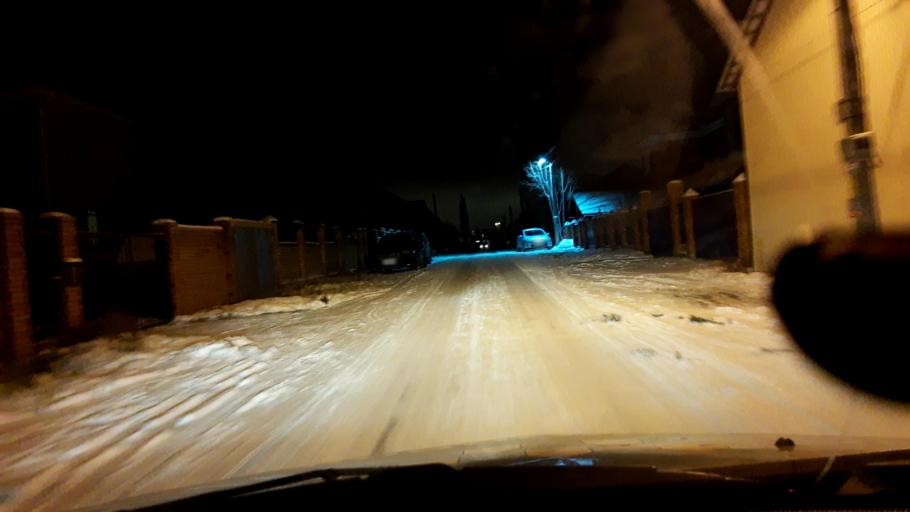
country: RU
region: Bashkortostan
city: Mikhaylovka
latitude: 54.8012
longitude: 55.9452
